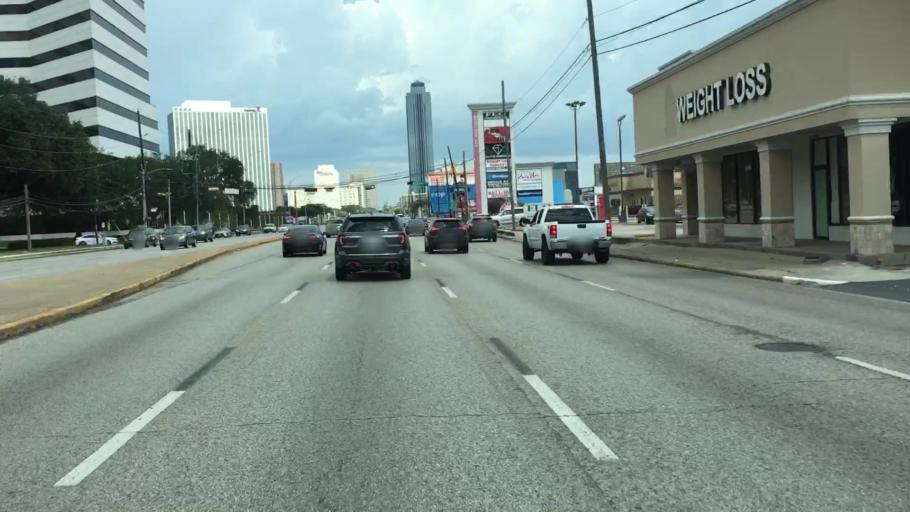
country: US
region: Texas
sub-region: Harris County
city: Hunters Creek Village
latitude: 29.7380
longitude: -95.4805
